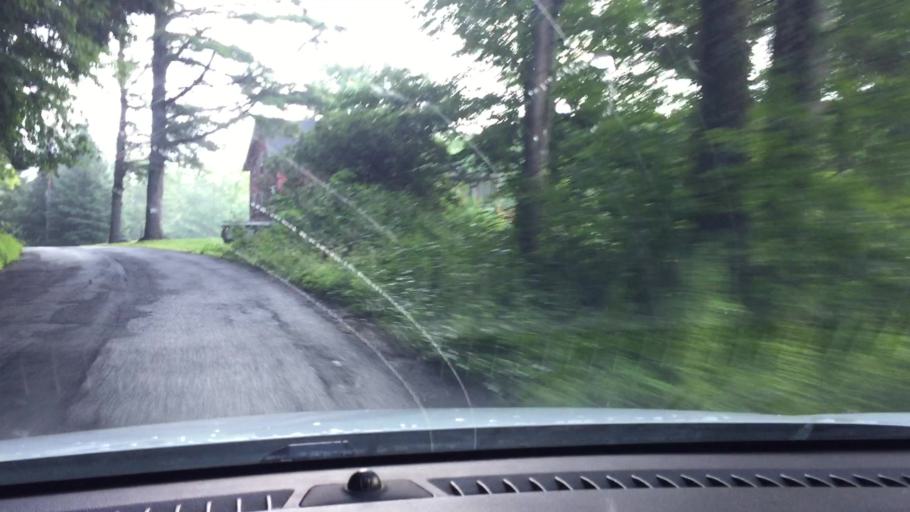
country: US
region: Massachusetts
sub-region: Hampshire County
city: Chesterfield
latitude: 42.3305
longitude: -72.9327
